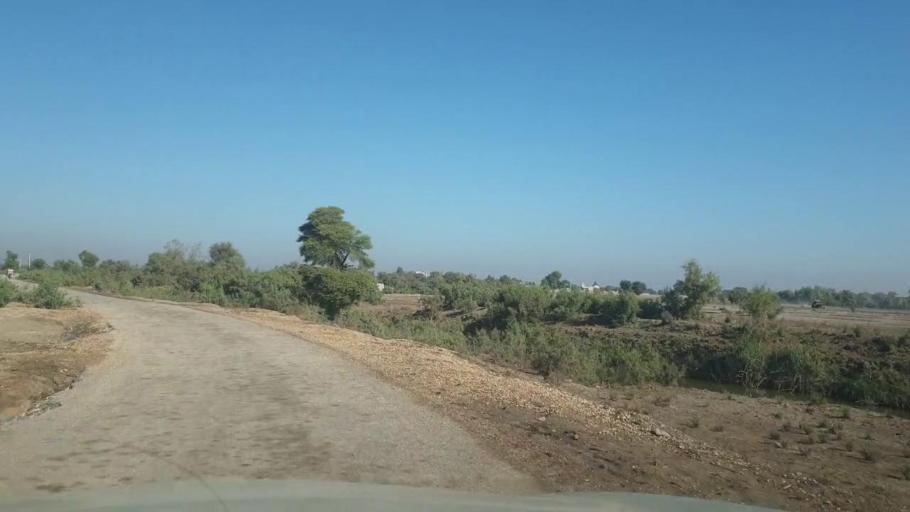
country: PK
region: Sindh
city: Bhan
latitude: 26.5372
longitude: 67.6588
